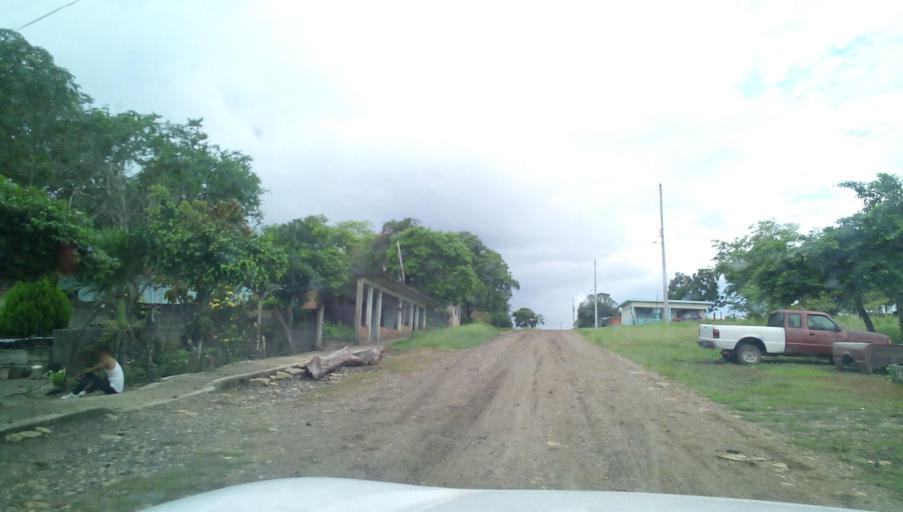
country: MX
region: Veracruz
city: Panuco
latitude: 21.8014
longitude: -98.1056
